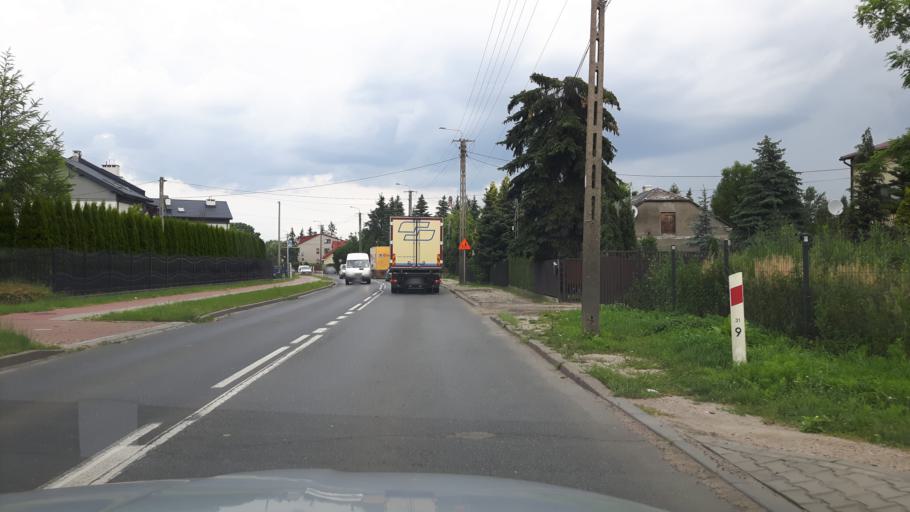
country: PL
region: Masovian Voivodeship
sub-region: Powiat wolominski
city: Nowe Lipiny
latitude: 52.3457
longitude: 21.2664
